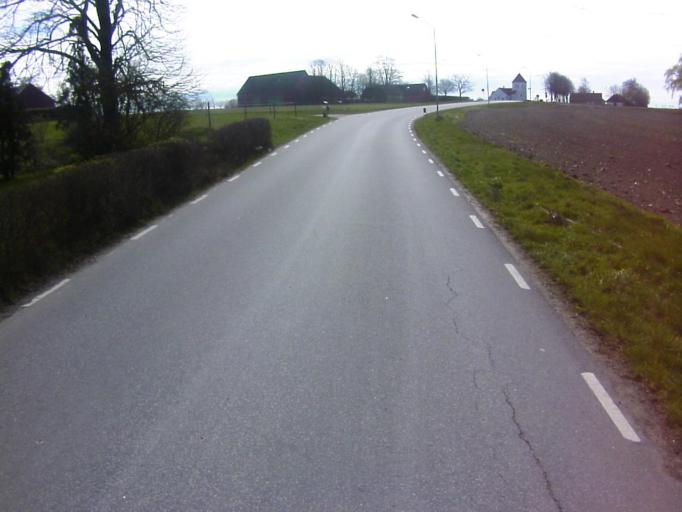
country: SE
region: Skane
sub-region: Kavlinge Kommun
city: Hofterup
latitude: 55.7869
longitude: 12.9742
